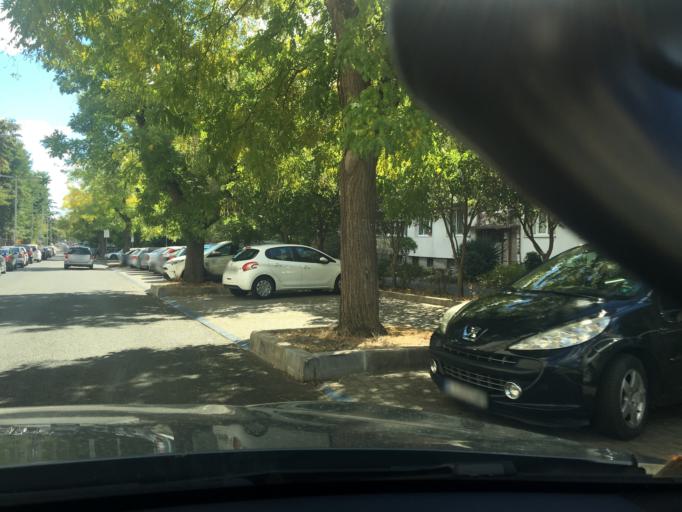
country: BG
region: Burgas
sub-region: Obshtina Burgas
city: Burgas
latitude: 42.5004
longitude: 27.4711
